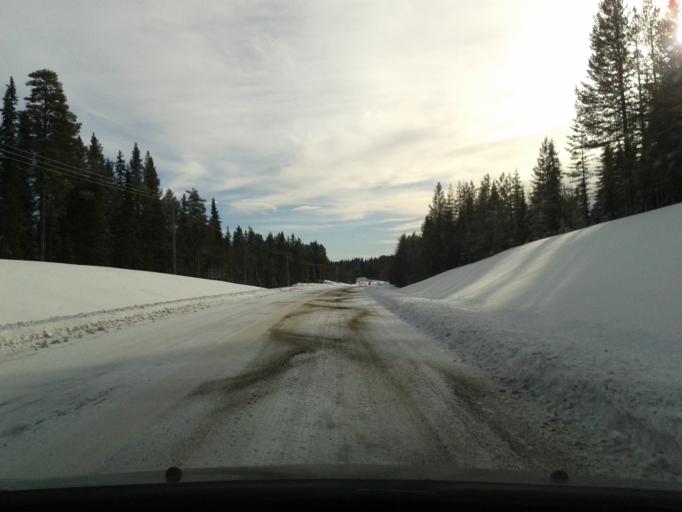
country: SE
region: Vaesterbotten
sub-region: Vilhelmina Kommun
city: Vilhelmina
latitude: 64.5453
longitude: 16.7454
